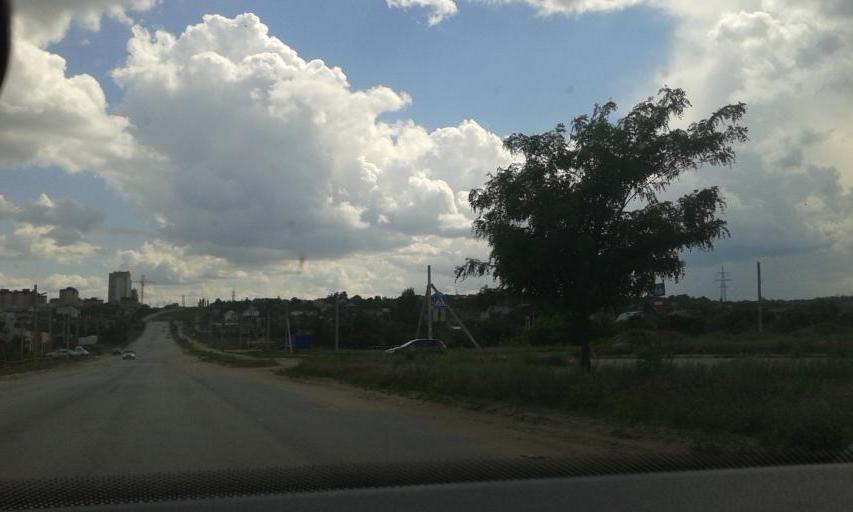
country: RU
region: Volgograd
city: Volgograd
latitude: 48.6563
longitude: 44.4137
